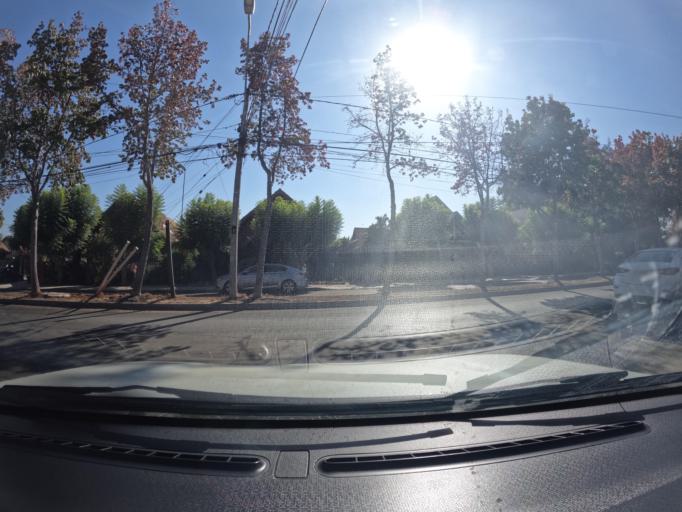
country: CL
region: Santiago Metropolitan
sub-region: Provincia de Santiago
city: Villa Presidente Frei, Nunoa, Santiago, Chile
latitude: -33.4842
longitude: -70.5619
